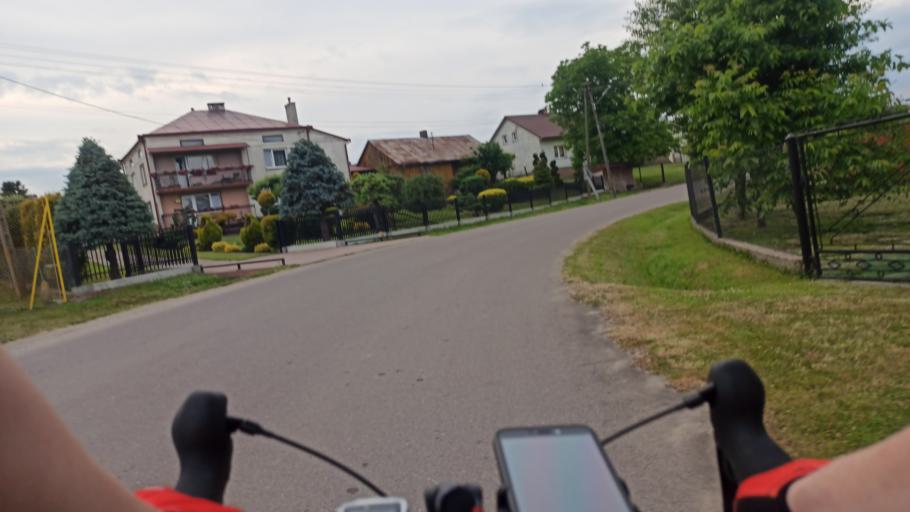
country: PL
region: Subcarpathian Voivodeship
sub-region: Powiat jaroslawski
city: Radymno
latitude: 49.9191
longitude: 22.8004
